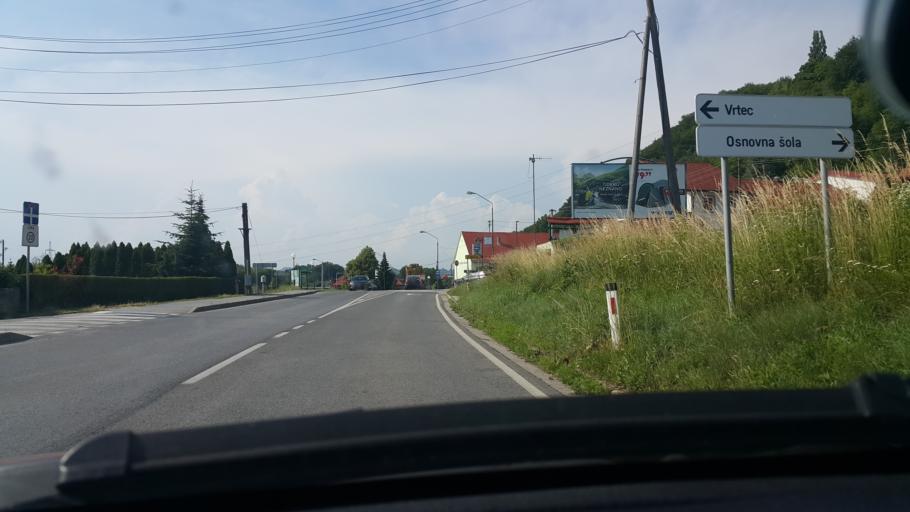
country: SI
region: Duplek
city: Zgornji Duplek
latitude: 46.5135
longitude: 15.7186
